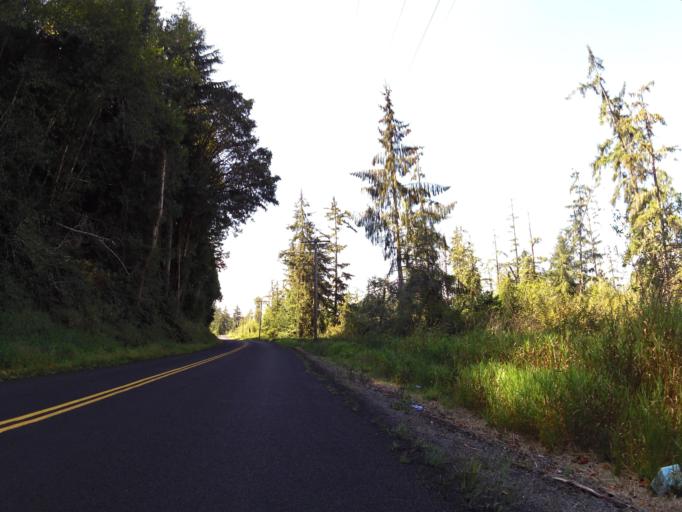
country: US
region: Washington
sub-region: Wahkiakum County
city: Cathlamet
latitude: 46.1965
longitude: -123.5685
